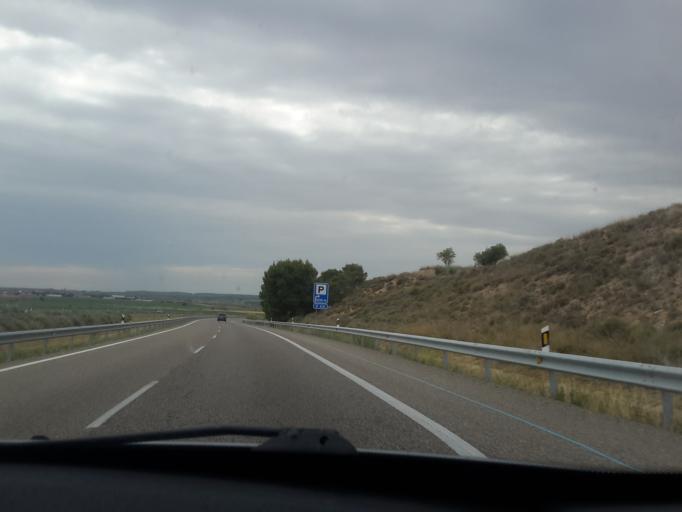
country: ES
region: Aragon
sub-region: Provincia de Huesca
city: Candasnos
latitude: 41.5043
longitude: 0.1057
